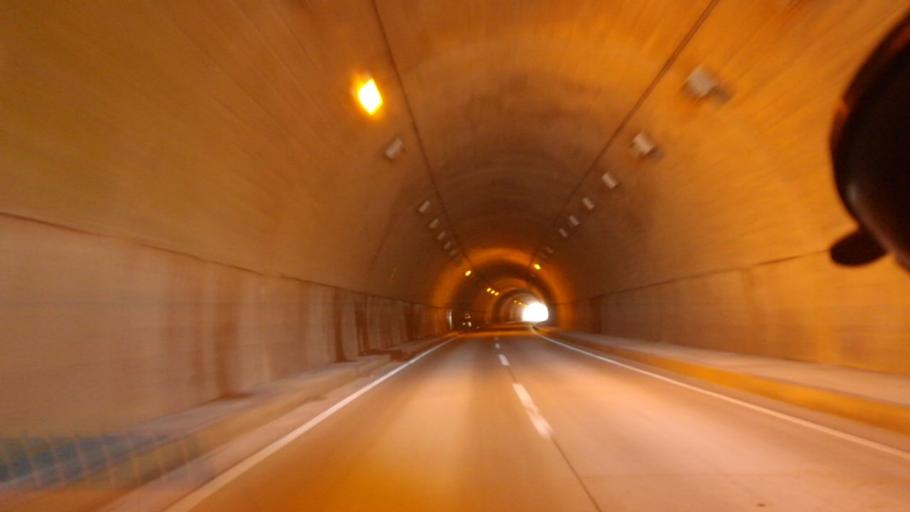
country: JP
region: Yamanashi
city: Uenohara
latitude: 35.5364
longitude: 139.2257
